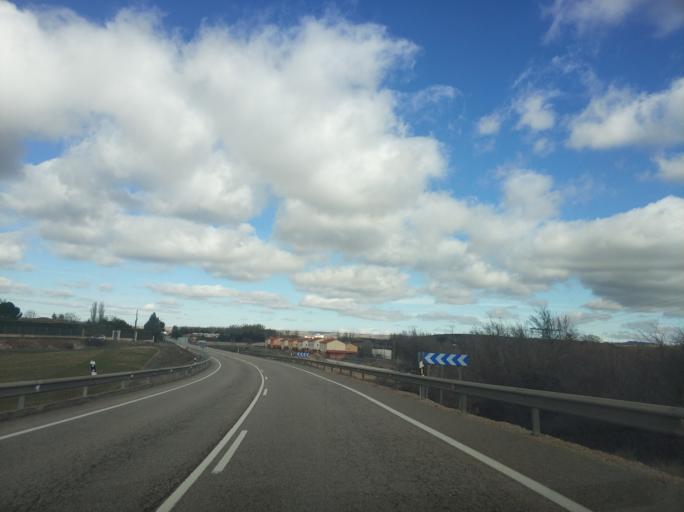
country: ES
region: Castille and Leon
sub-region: Provincia de Burgos
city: Revillarruz
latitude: 42.2254
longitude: -3.6554
